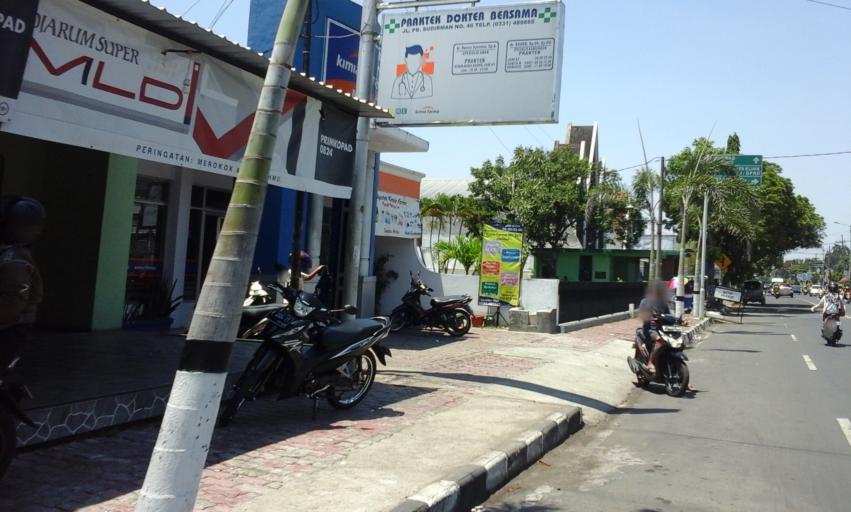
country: ID
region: East Java
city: Krajan
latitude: -8.1654
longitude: 113.7054
